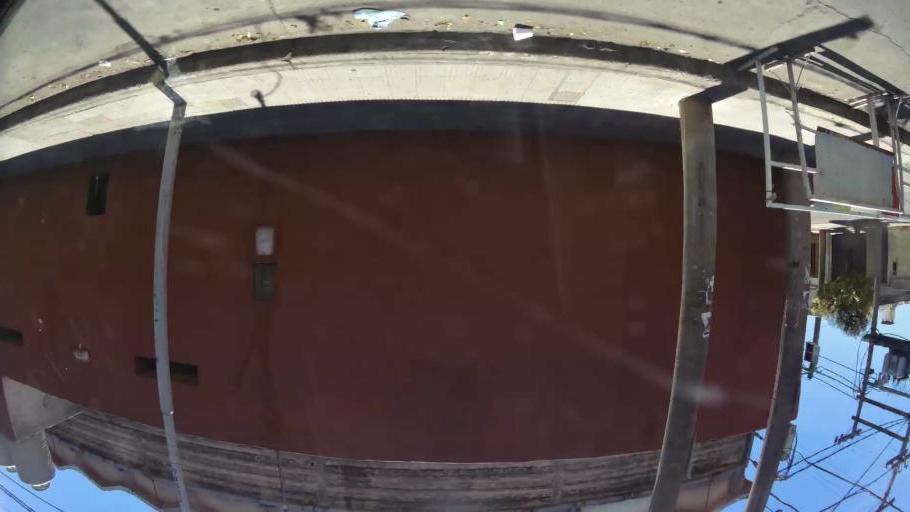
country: AR
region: Cordoba
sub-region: Departamento de Capital
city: Cordoba
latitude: -31.3864
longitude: -64.1348
